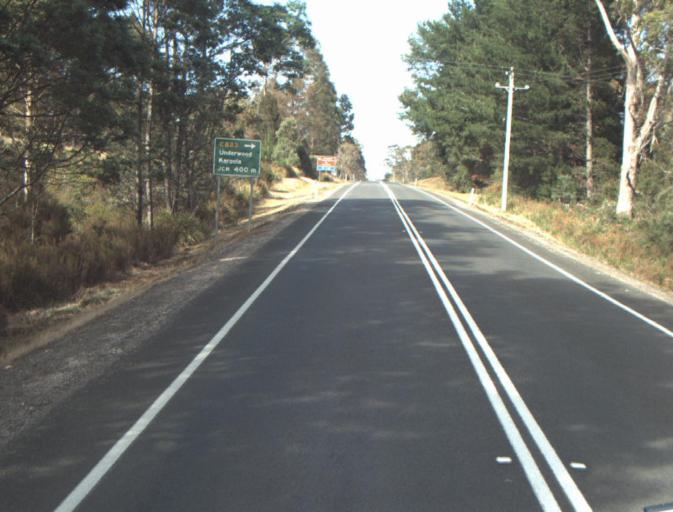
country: AU
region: Tasmania
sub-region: Launceston
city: Mayfield
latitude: -41.3097
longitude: 147.2021
